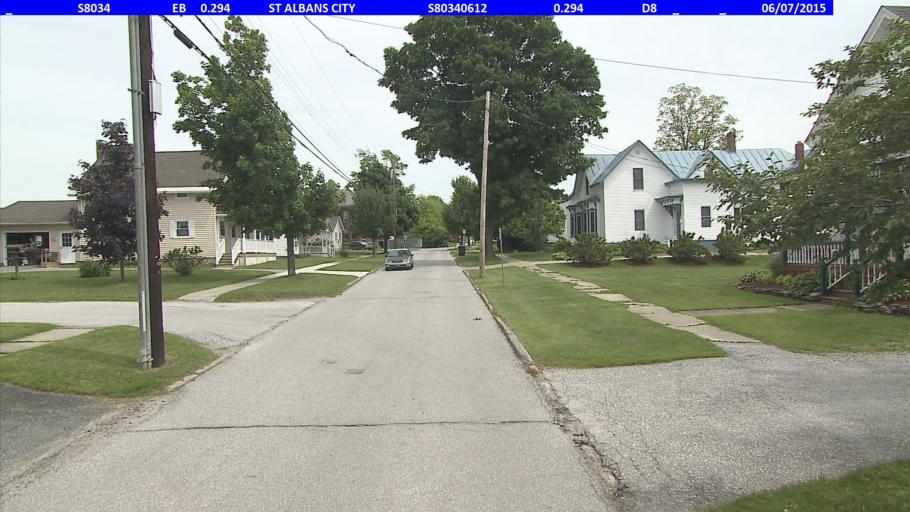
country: US
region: Vermont
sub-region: Franklin County
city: Saint Albans
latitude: 44.8052
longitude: -73.0796
